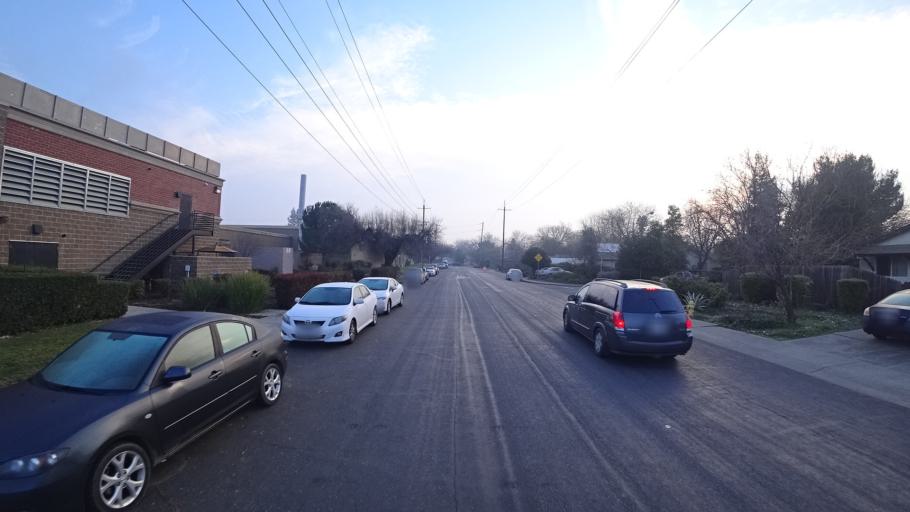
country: US
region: California
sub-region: Yolo County
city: Davis
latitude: 38.5606
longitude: -121.7330
